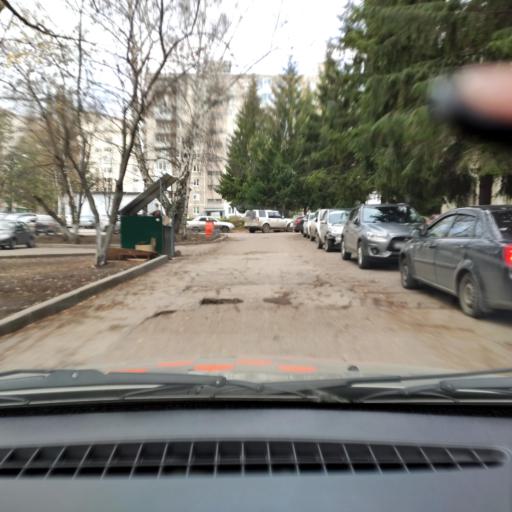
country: RU
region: Bashkortostan
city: Ufa
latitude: 54.7592
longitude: 56.0193
